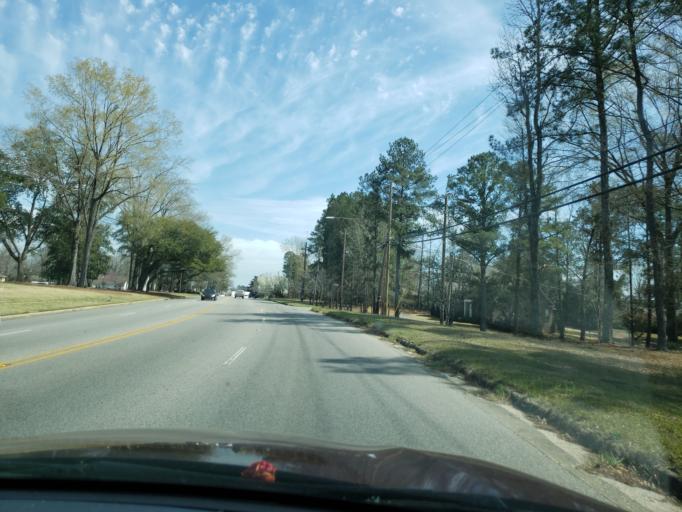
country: US
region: Alabama
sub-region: Elmore County
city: Tallassee
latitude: 32.5444
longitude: -85.9097
